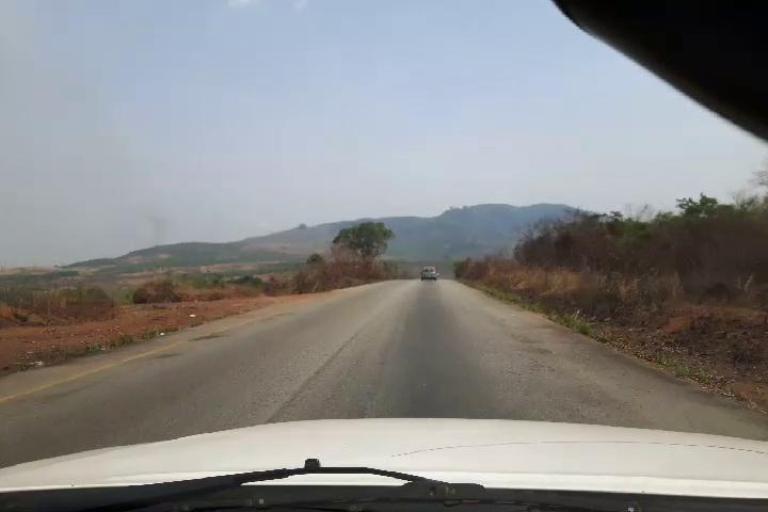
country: SL
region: Northern Province
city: Yonibana
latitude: 8.3897
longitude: -12.1912
